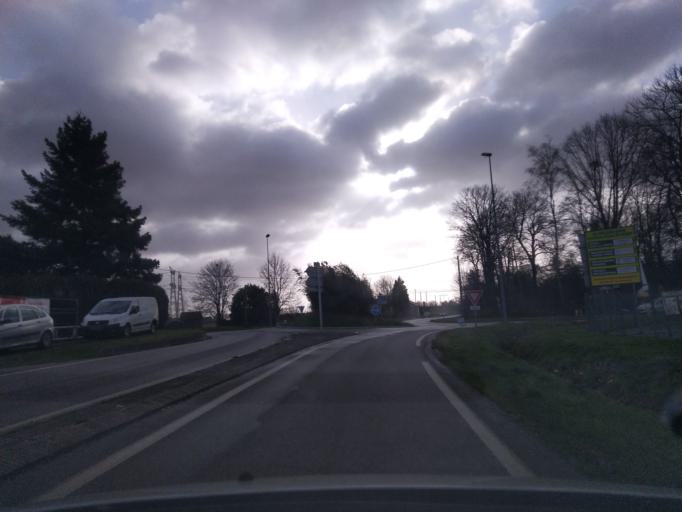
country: FR
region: Haute-Normandie
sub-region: Departement de la Seine-Maritime
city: Pissy-Poville
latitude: 49.5203
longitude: 0.9883
